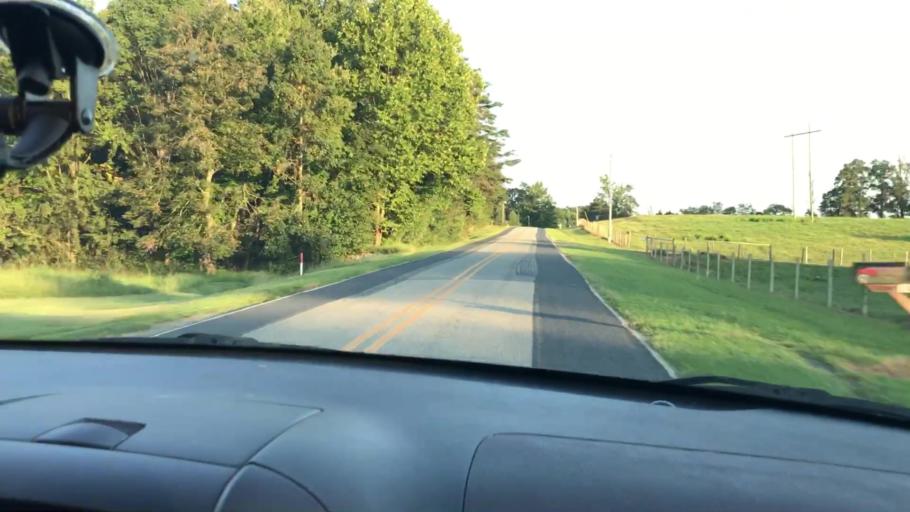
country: US
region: North Carolina
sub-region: Randolph County
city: Ramseur
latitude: 35.7786
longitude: -79.6330
